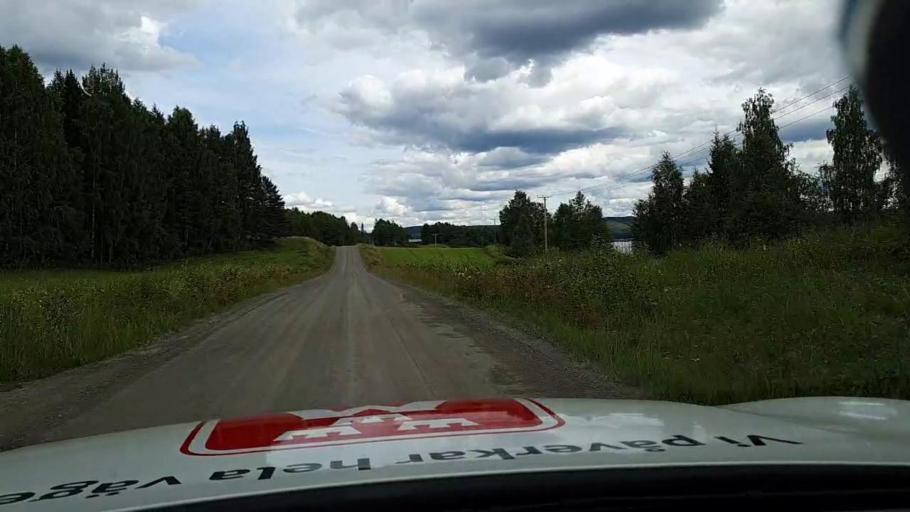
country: SE
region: Jaemtland
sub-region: Braecke Kommun
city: Braecke
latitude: 63.1971
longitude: 15.4673
